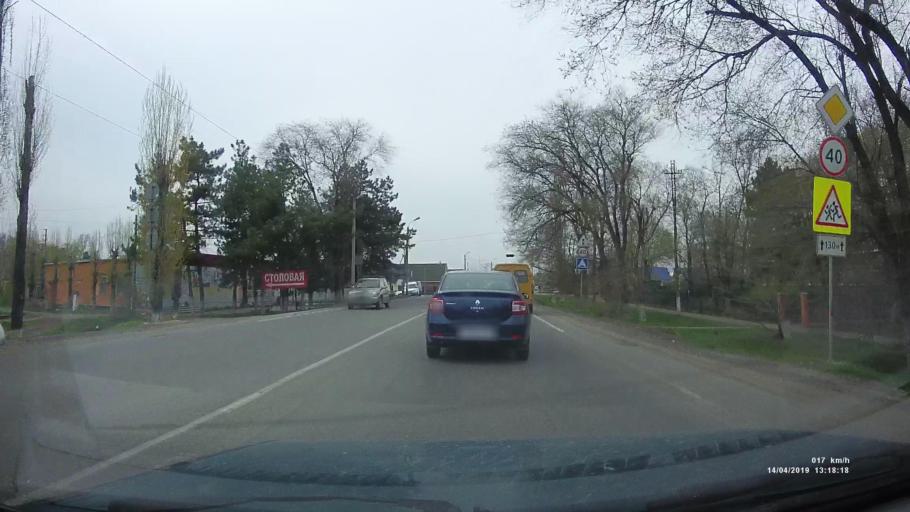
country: RU
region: Rostov
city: Kuleshovka
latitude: 47.0785
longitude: 39.5562
